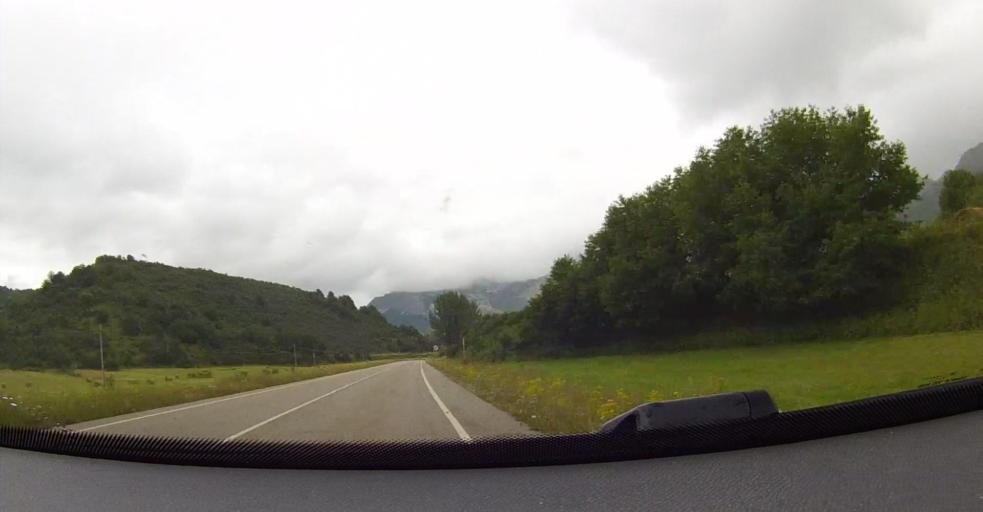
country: ES
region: Castille and Leon
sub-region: Provincia de Leon
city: Buron
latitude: 43.0377
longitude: -5.0823
